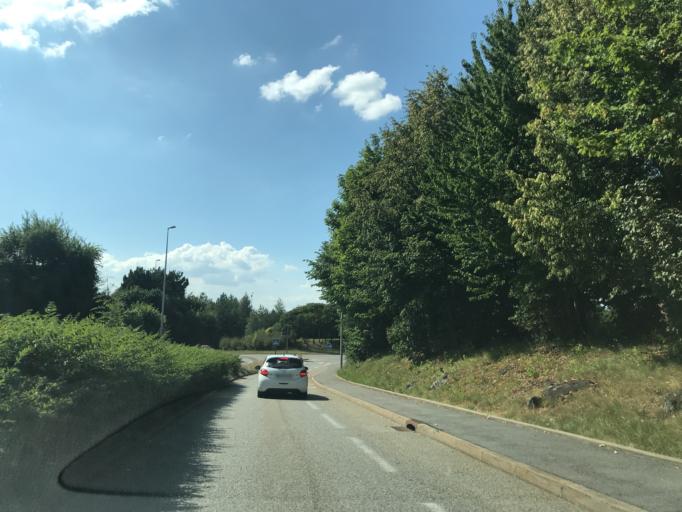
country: FR
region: Rhone-Alpes
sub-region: Departement de la Haute-Savoie
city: Villaz
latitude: 45.9230
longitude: 6.1751
